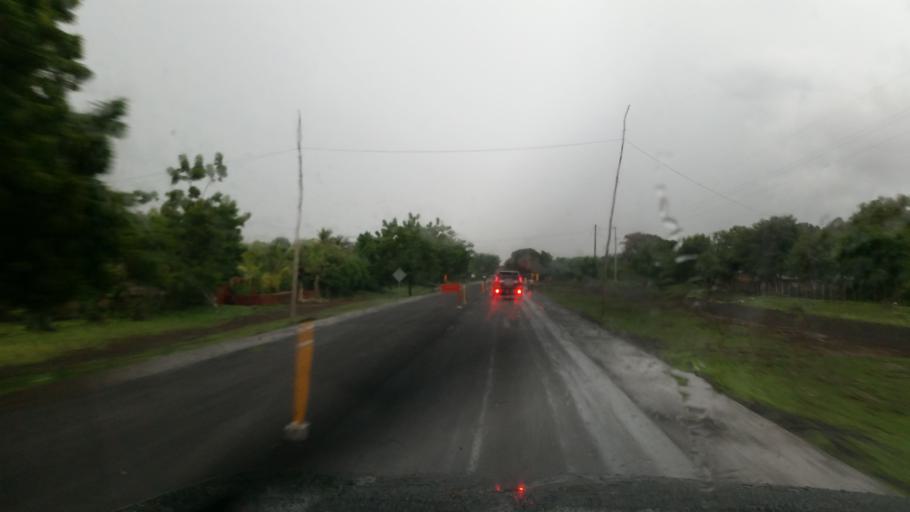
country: NI
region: Chinandega
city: Chichigalpa
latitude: 12.7883
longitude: -86.9495
